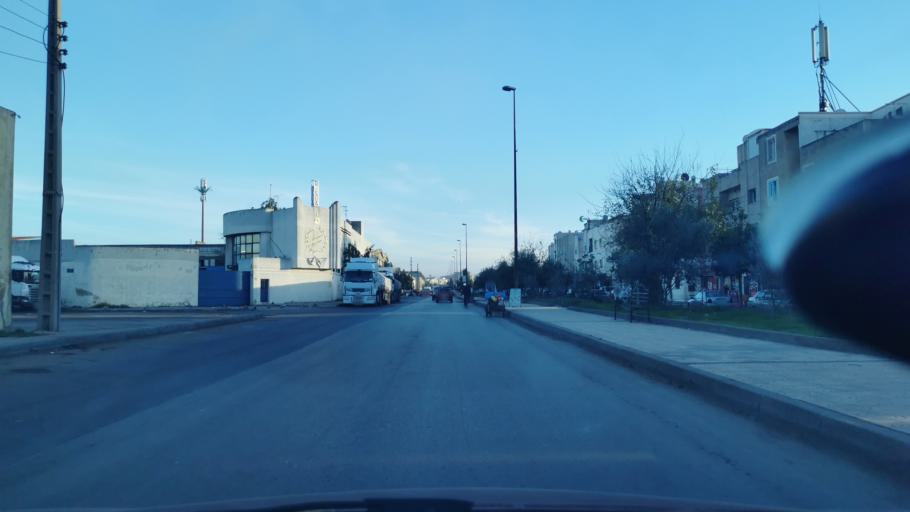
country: MA
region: Fes-Boulemane
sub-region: Fes
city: Fes
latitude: 34.0256
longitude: -4.9858
